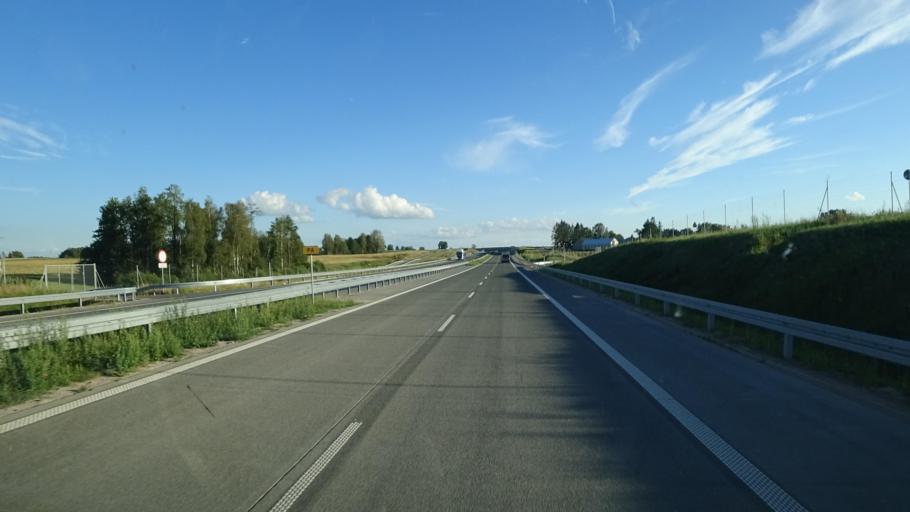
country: PL
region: Podlasie
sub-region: Powiat suwalski
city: Raczki
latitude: 53.9490
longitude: 22.7663
